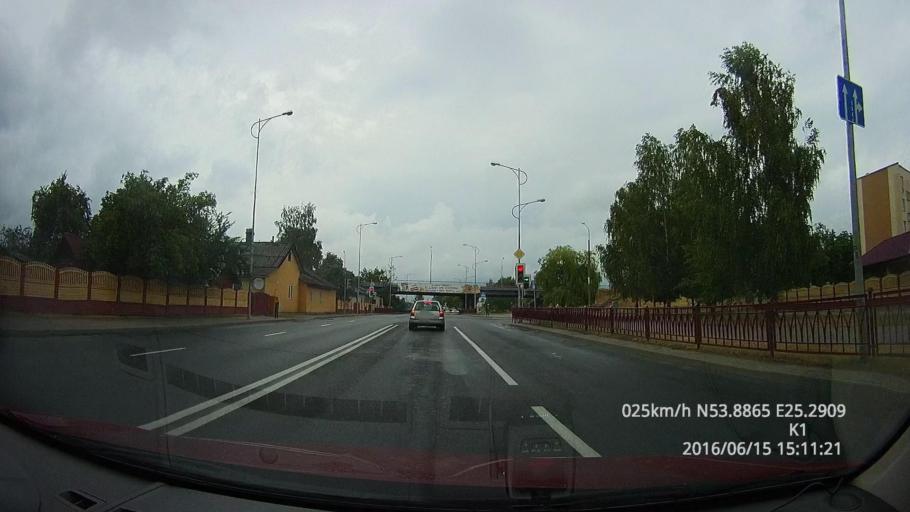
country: BY
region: Grodnenskaya
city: Lida
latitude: 53.8866
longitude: 25.2908
